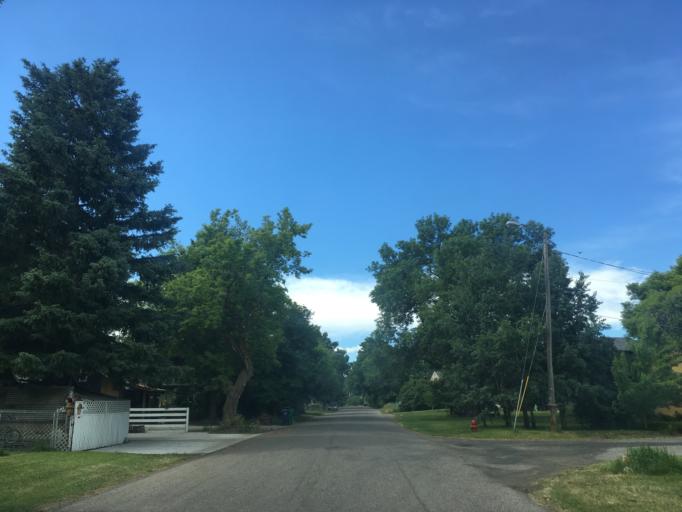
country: US
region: Montana
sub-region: Gallatin County
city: Bozeman
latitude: 45.6839
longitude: -111.0258
